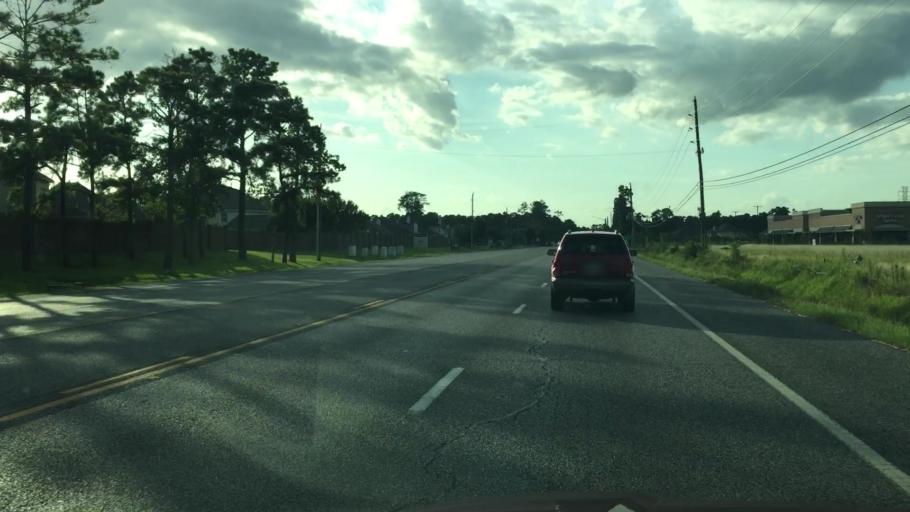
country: US
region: Texas
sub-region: Harris County
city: Tomball
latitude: 30.0773
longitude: -95.5591
